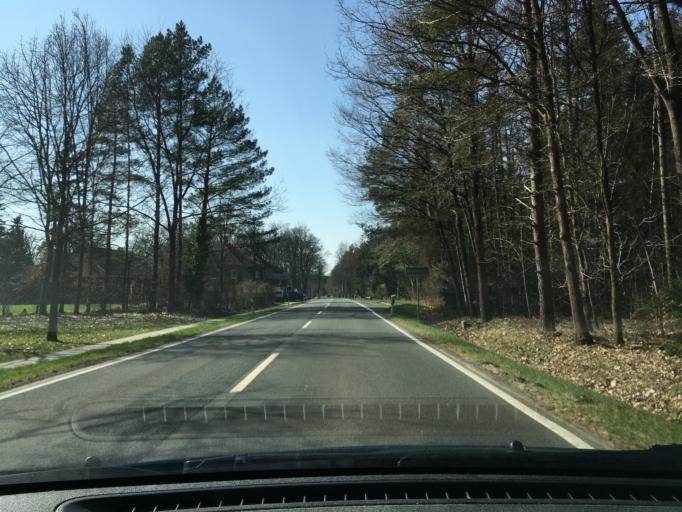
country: DE
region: Lower Saxony
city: Hermannsburg
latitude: 52.8249
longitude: 10.1226
